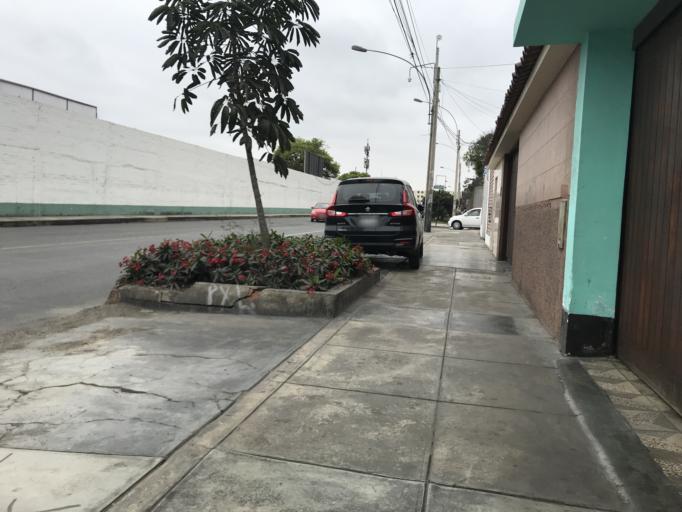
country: PE
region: Callao
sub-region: Callao
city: Callao
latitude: -12.0736
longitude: -77.0760
